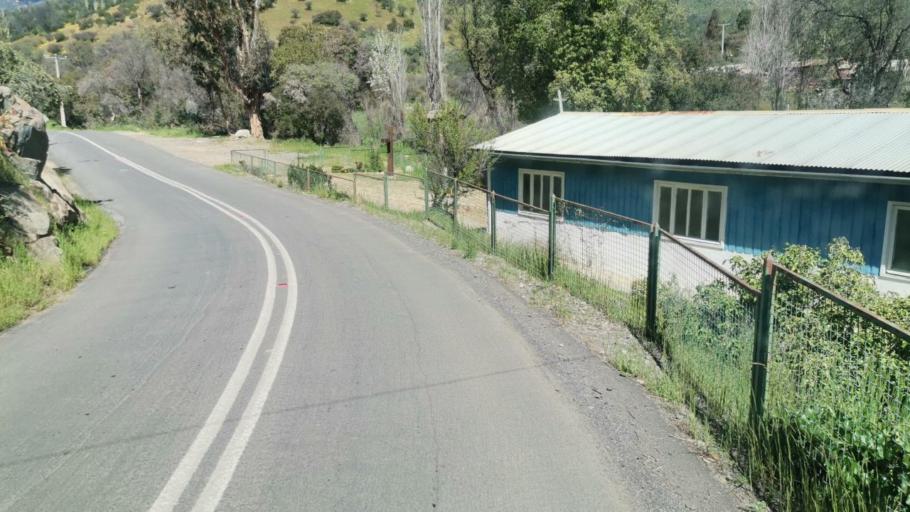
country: CL
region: Valparaiso
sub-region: Provincia de Marga Marga
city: Limache
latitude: -33.1821
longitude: -71.1109
